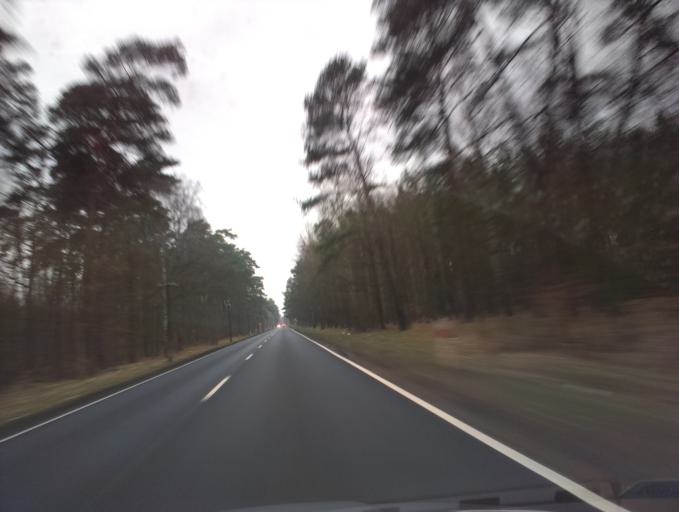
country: PL
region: Greater Poland Voivodeship
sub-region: Powiat zlotowski
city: Jastrowie
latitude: 53.3857
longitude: 16.7911
